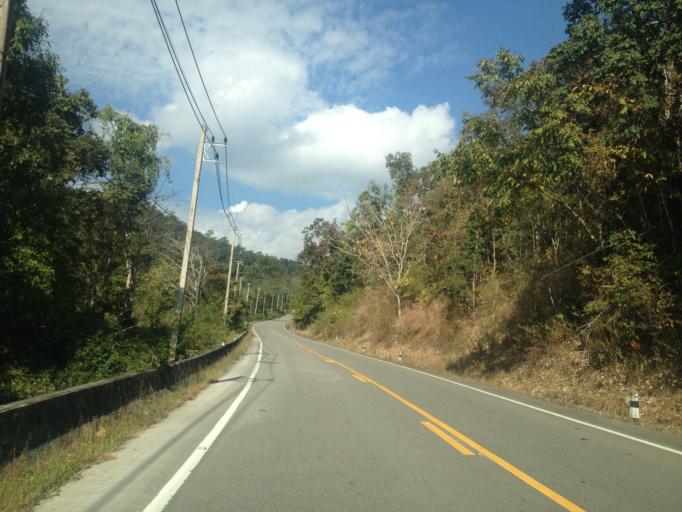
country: TH
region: Mae Hong Son
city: Ban Huai I Huak
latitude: 18.1357
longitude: 98.1772
